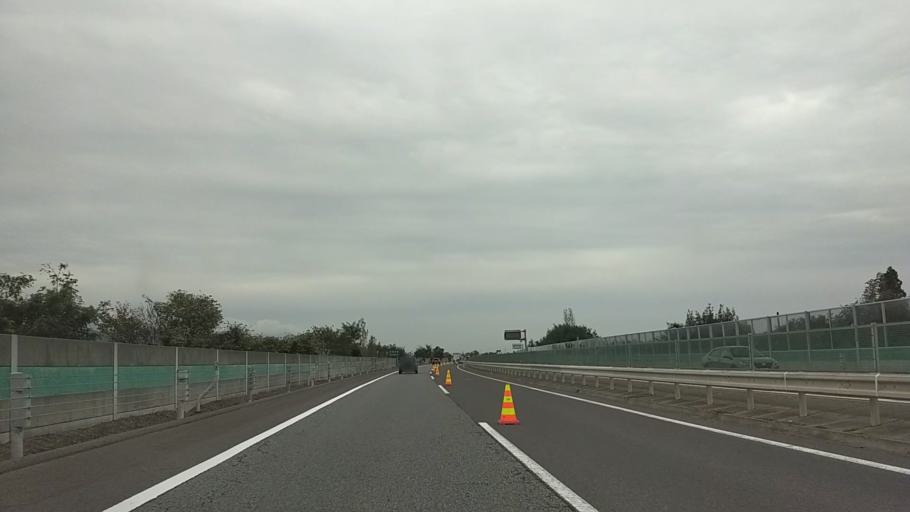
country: JP
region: Nagano
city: Toyoshina
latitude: 36.2951
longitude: 137.9269
